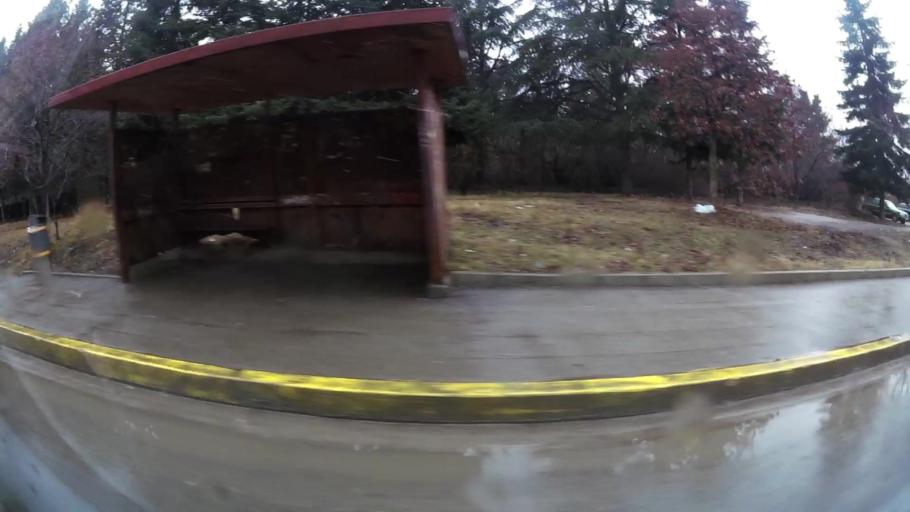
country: BG
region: Sofia-Capital
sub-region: Stolichna Obshtina
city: Sofia
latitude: 42.6381
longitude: 23.4065
